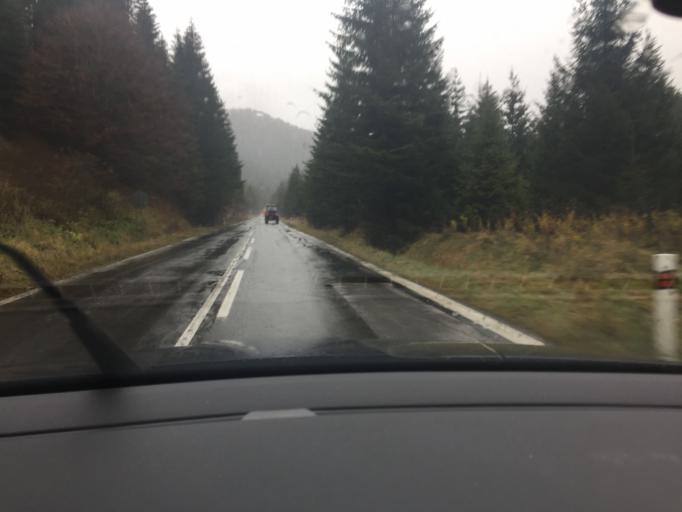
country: SK
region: Presovsky
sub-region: Okres Poprad
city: Zdiar
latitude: 49.2535
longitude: 20.3041
